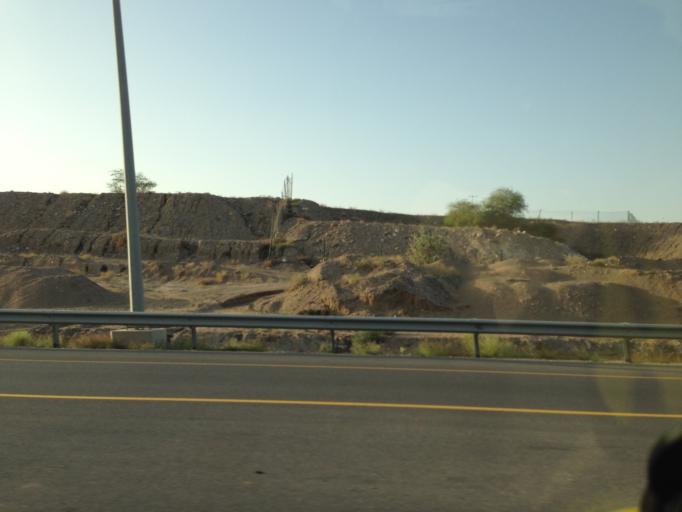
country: OM
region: Muhafazat Masqat
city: Bawshar
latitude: 23.5741
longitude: 58.4312
